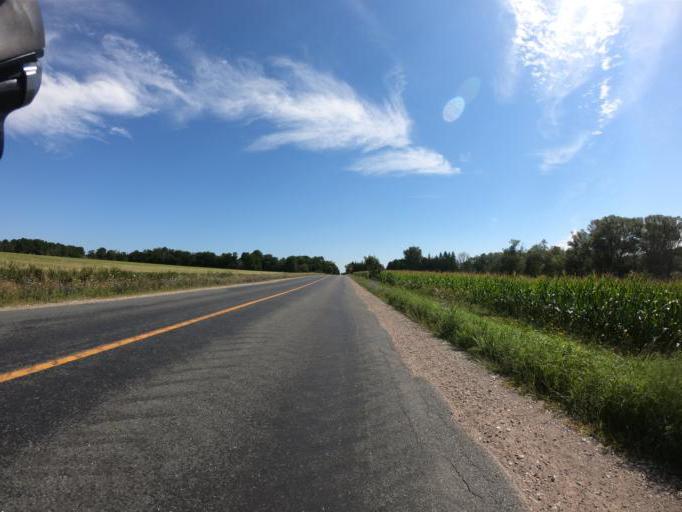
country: CA
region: Ontario
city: Waterloo
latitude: 43.5087
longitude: -80.3969
